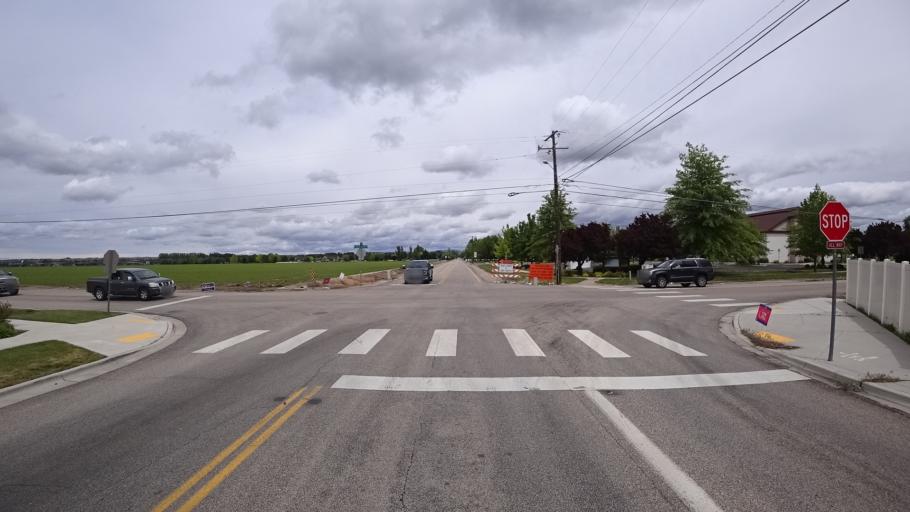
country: US
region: Idaho
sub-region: Ada County
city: Eagle
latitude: 43.7061
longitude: -116.4037
